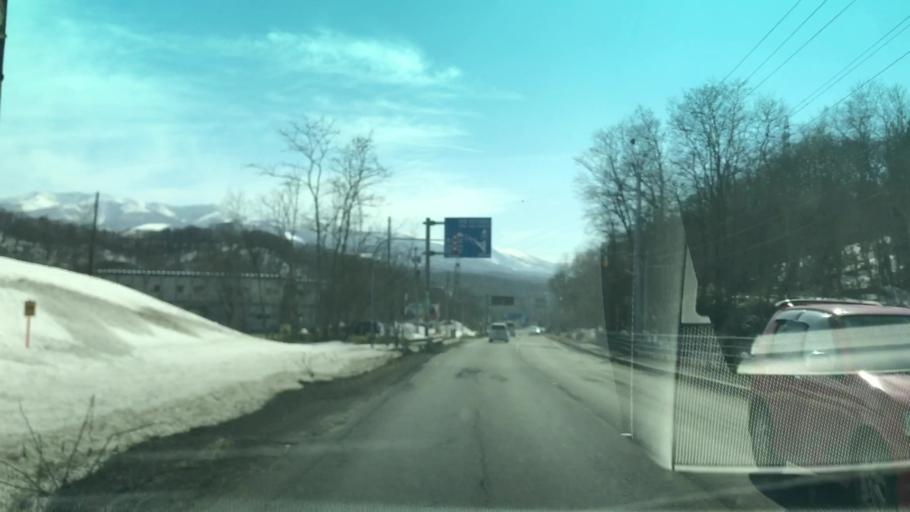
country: JP
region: Hokkaido
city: Iwanai
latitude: 42.9872
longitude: 140.6584
